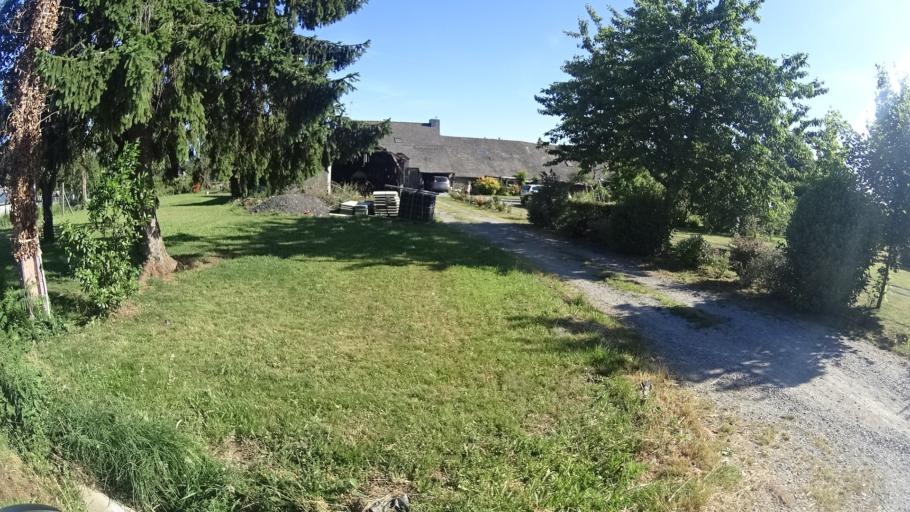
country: FR
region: Brittany
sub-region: Departement d'Ille-et-Vilaine
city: Sainte-Marie
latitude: 47.6821
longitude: -2.0040
